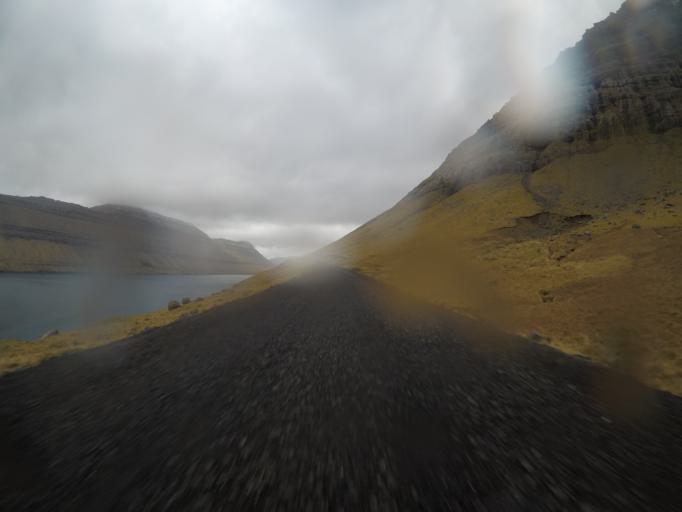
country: FO
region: Nordoyar
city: Klaksvik
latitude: 62.3323
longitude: -6.5744
